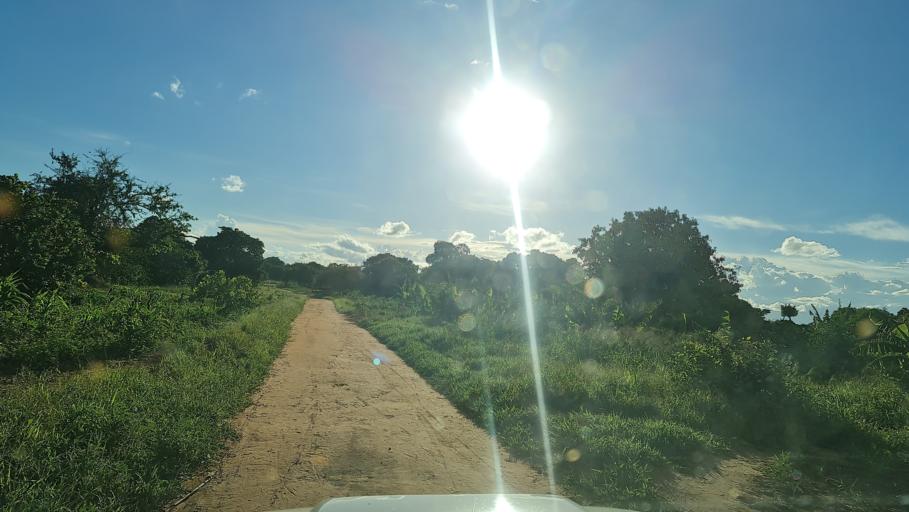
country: MZ
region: Nampula
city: Ilha de Mocambique
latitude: -14.9433
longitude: 40.1654
